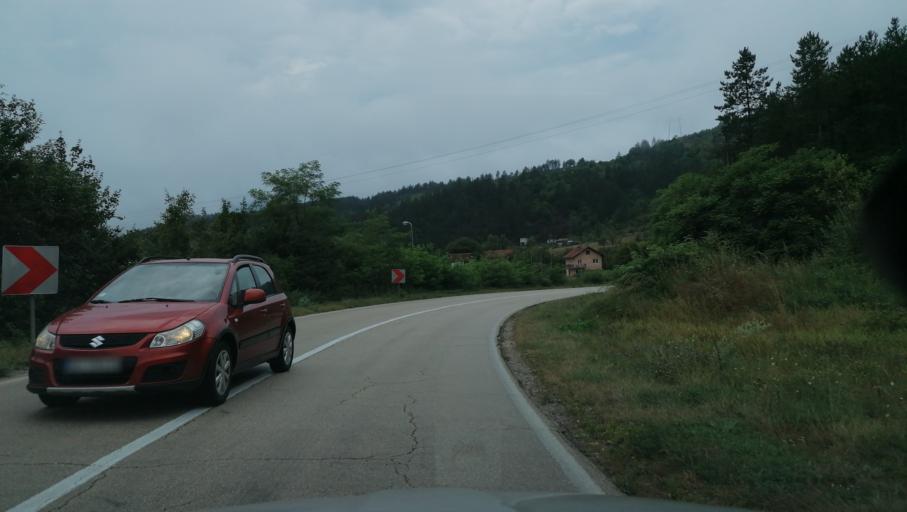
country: BA
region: Republika Srpska
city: Visegrad
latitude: 43.7865
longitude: 19.3327
